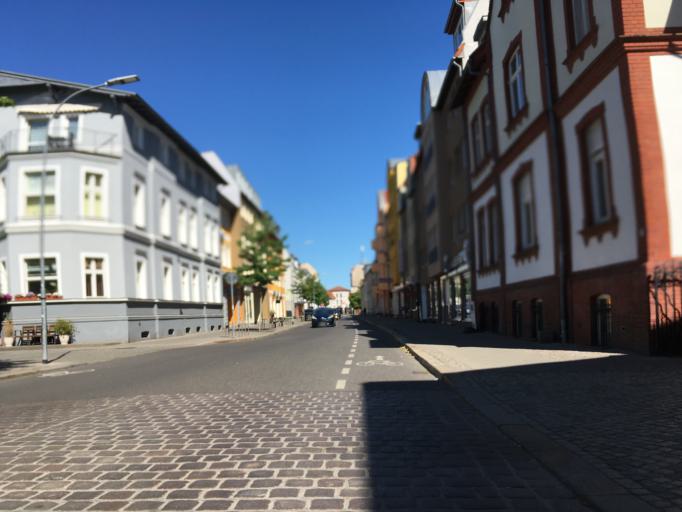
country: DE
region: Brandenburg
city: Oranienburg
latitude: 52.7542
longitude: 13.2434
